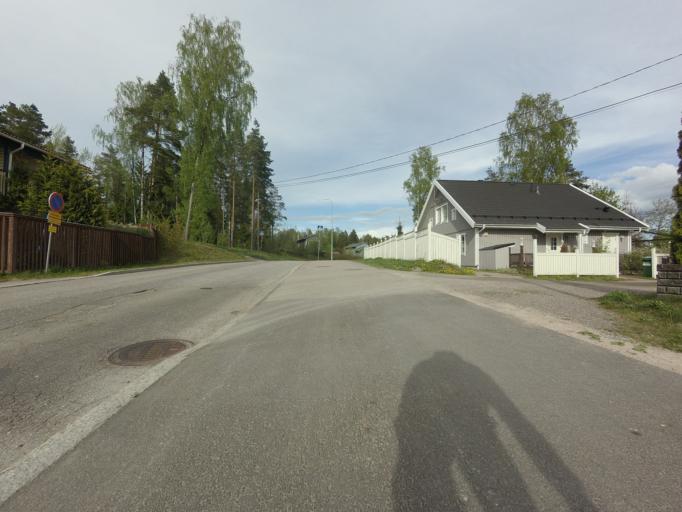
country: FI
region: Uusimaa
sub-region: Helsinki
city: Kauniainen
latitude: 60.1984
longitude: 24.7116
